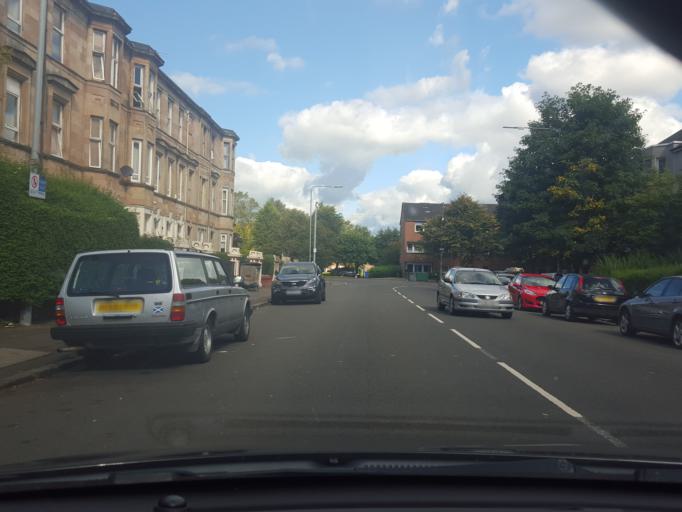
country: GB
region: Scotland
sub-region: Glasgow City
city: Glasgow
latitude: 55.8562
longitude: -4.3032
